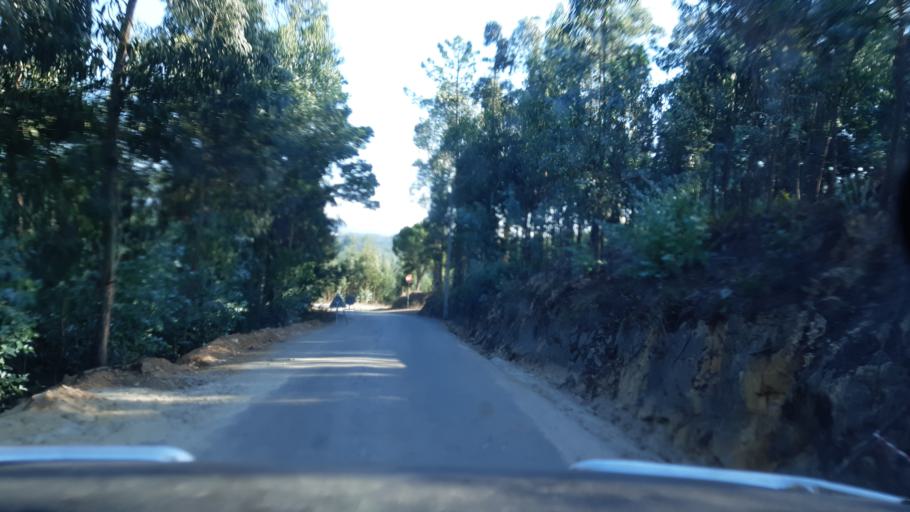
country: PT
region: Aveiro
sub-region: Agueda
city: Aguada de Cima
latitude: 40.5687
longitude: -8.3639
